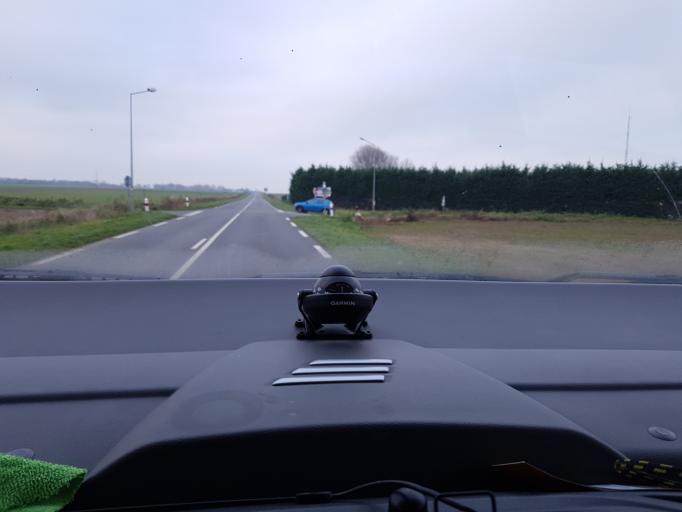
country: FR
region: Picardie
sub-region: Departement de la Somme
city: Ault
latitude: 50.0882
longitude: 1.4524
